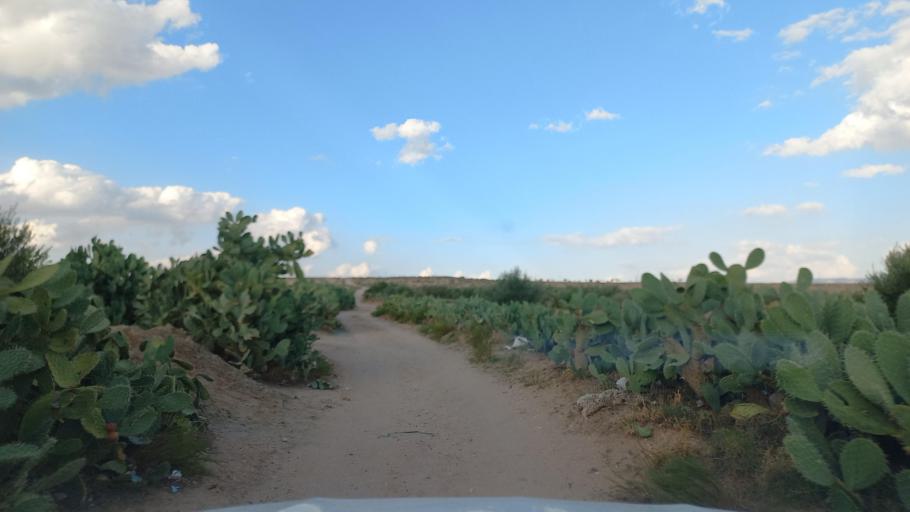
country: TN
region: Al Qasrayn
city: Sbiba
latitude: 35.3867
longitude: 9.0532
